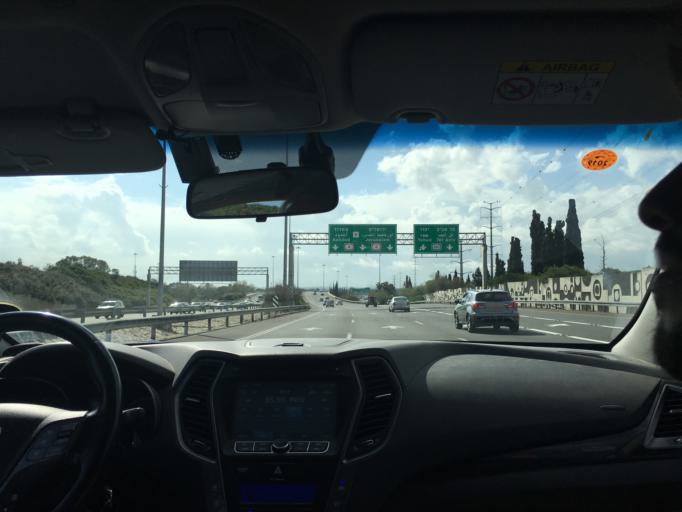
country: IL
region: Tel Aviv
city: Azor
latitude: 32.0428
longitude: 34.8296
